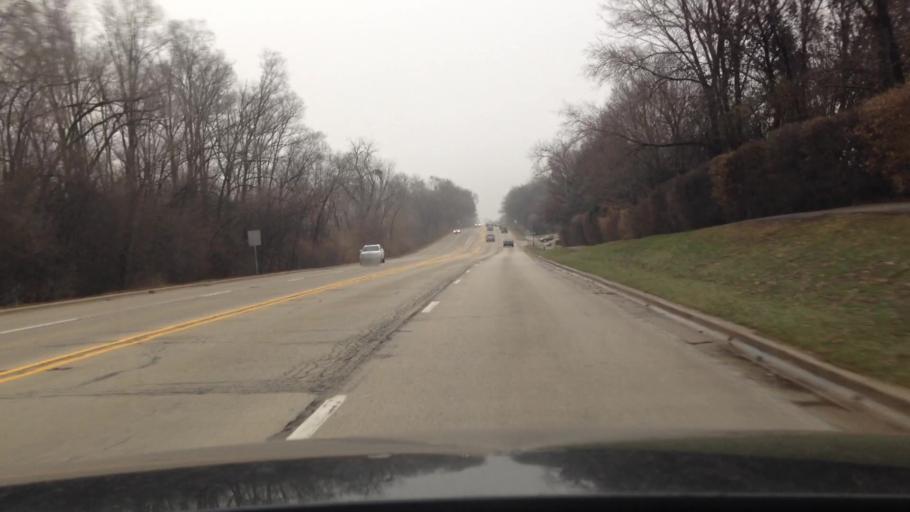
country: US
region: Illinois
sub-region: DuPage County
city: Oakbrook Terrace
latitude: 41.8314
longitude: -87.9828
